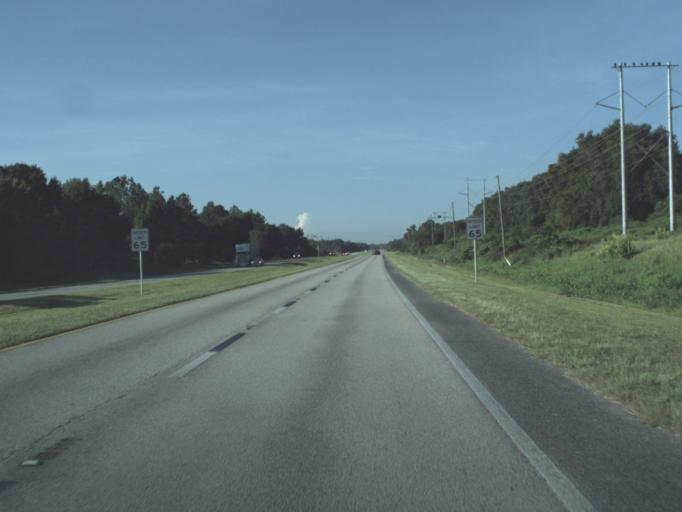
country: US
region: Florida
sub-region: Polk County
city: Fort Meade
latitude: 27.7198
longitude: -81.8028
